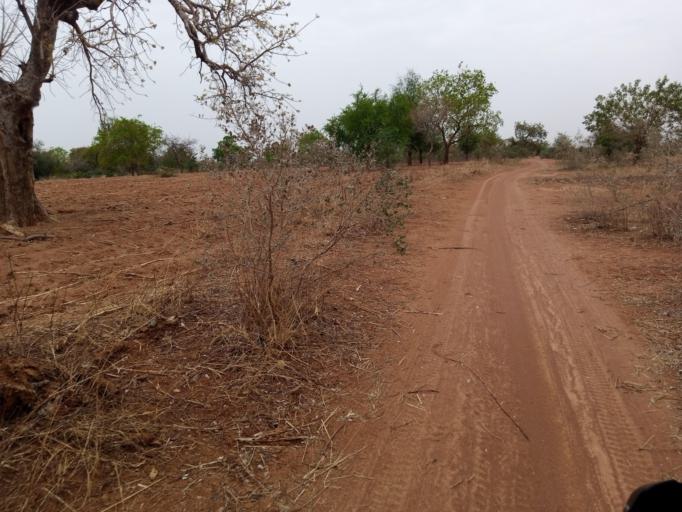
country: BF
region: Boucle du Mouhoun
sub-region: Province de la Kossi
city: Nouna
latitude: 12.8371
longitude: -4.0769
